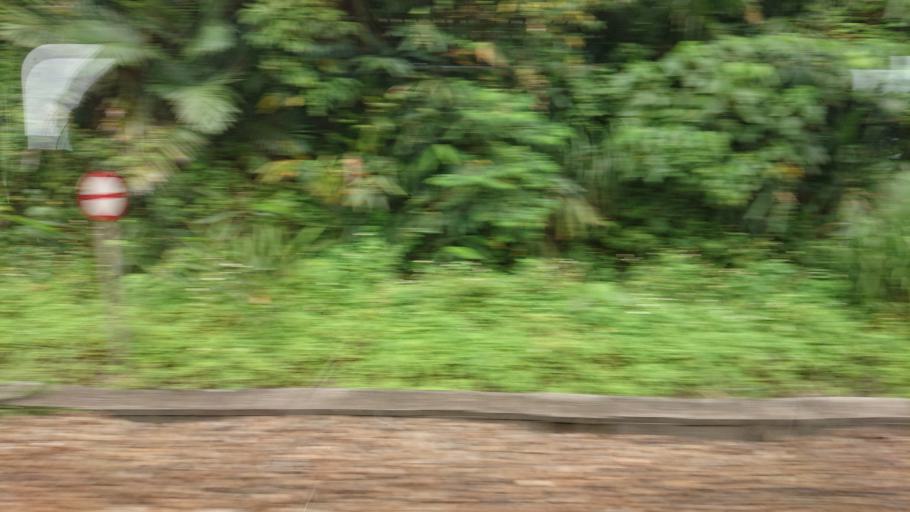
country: TW
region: Taiwan
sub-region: Keelung
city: Keelung
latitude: 24.9610
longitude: 121.9194
